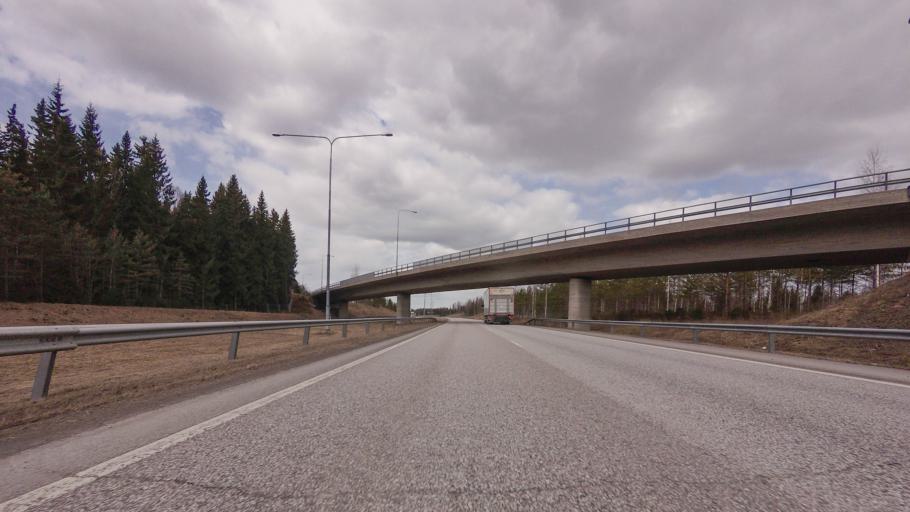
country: FI
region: Uusimaa
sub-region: Helsinki
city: Hyvinge
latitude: 60.5531
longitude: 24.8340
